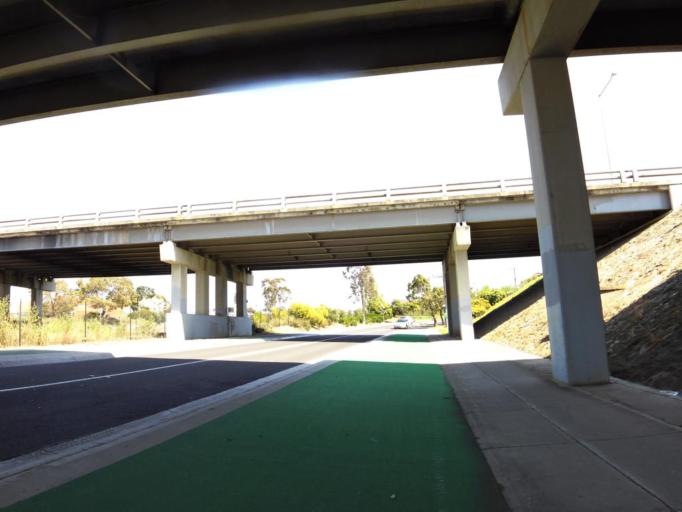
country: AU
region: Victoria
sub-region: Moreland
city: Gowanbrae
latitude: -37.7098
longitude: 144.8910
